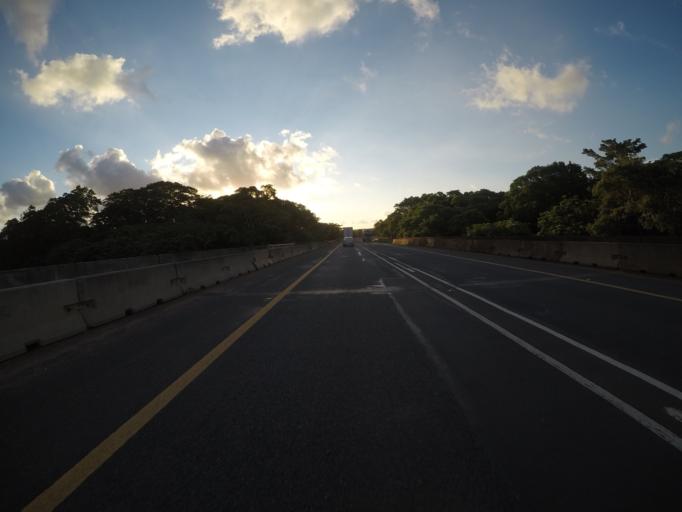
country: ZA
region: KwaZulu-Natal
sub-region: uThungulu District Municipality
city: Richards Bay
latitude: -28.6963
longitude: 32.0135
